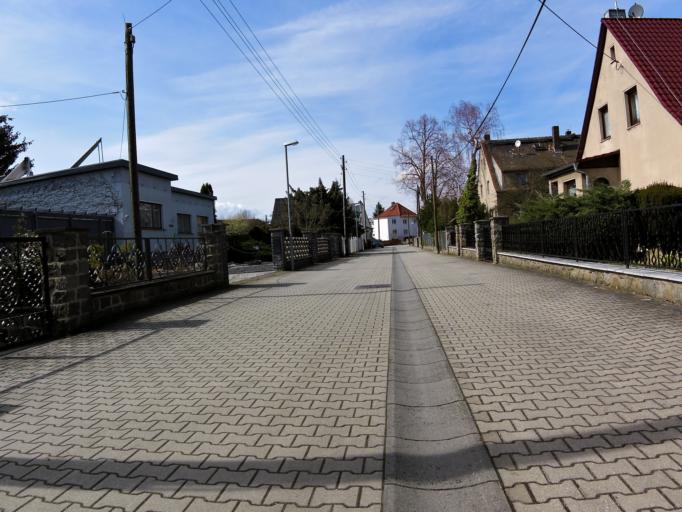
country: DE
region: Saxony
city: Taucha
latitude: 51.3392
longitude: 12.4876
